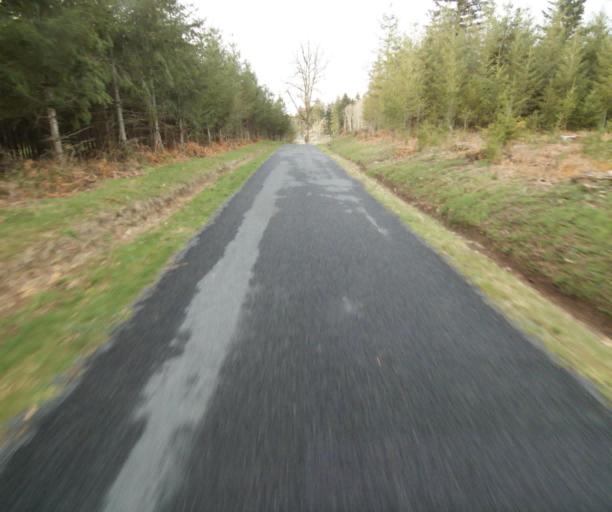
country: FR
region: Limousin
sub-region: Departement de la Correze
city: Argentat
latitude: 45.2172
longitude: 1.9405
